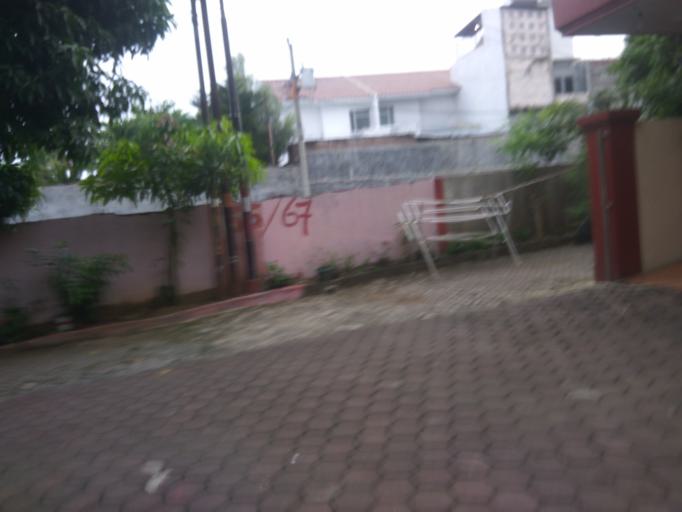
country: ID
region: Central Java
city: Mranggen
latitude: -7.0254
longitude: 110.4636
